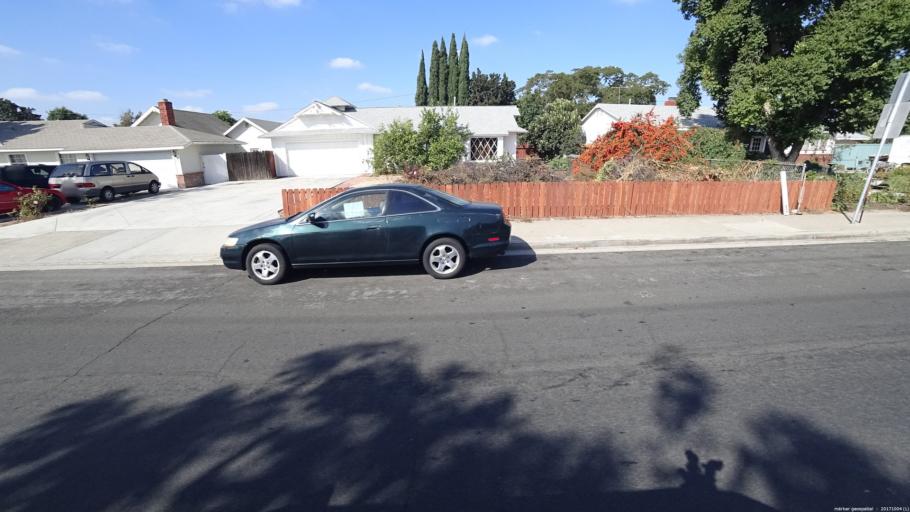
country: US
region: California
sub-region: Orange County
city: Garden Grove
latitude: 33.7879
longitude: -117.9324
